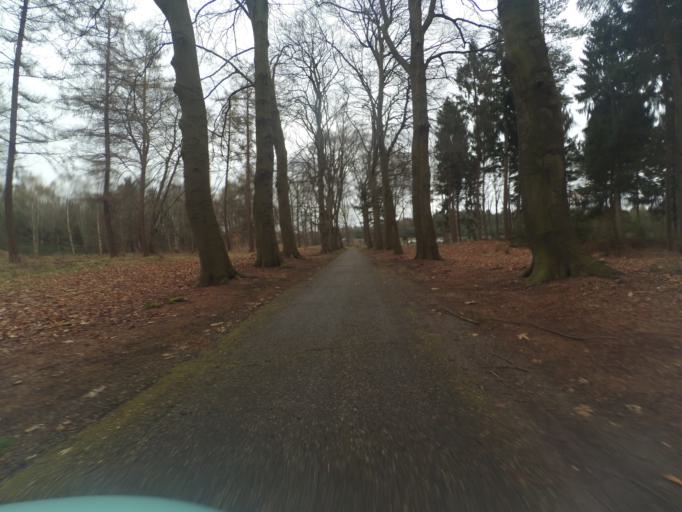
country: NL
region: Gelderland
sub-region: Gemeente Arnhem
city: Gulden Bodem
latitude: 52.0187
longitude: 5.9175
